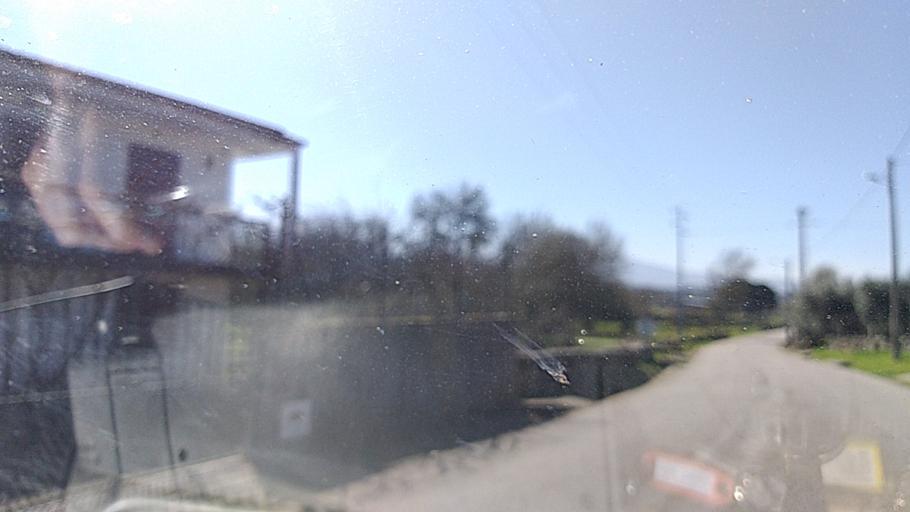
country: PT
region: Guarda
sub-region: Fornos de Algodres
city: Fornos de Algodres
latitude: 40.5946
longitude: -7.4707
